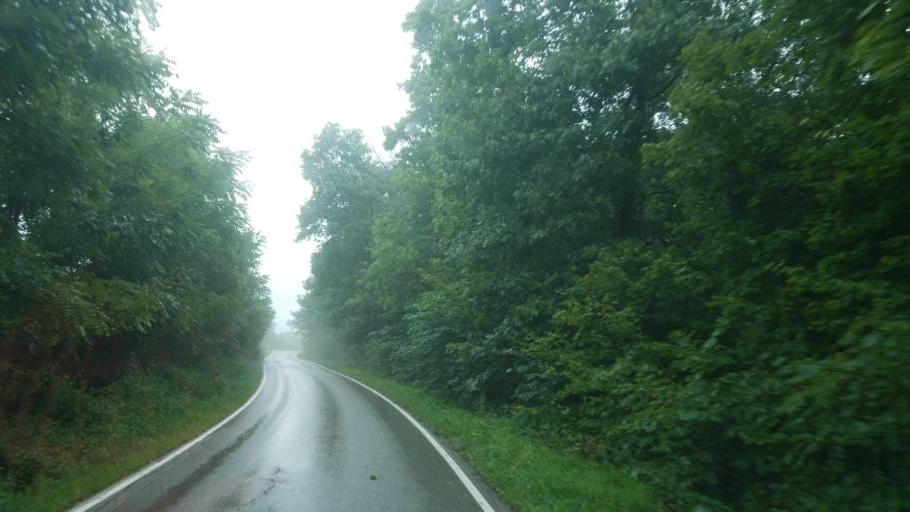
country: US
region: Kentucky
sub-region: Fleming County
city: Flemingsburg
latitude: 38.4737
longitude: -83.5128
